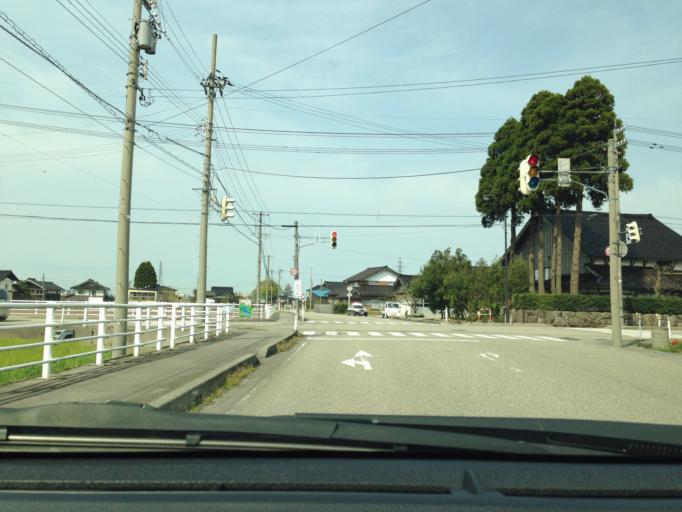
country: JP
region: Toyama
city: Fukumitsu
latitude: 36.5444
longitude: 136.8699
